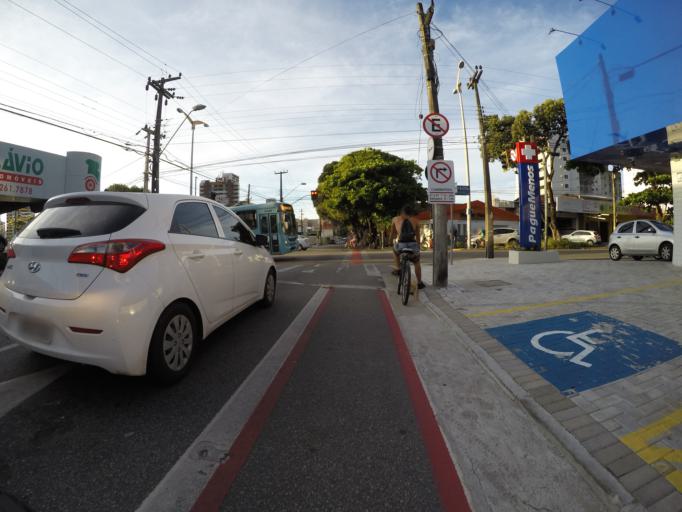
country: BR
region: Ceara
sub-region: Fortaleza
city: Fortaleza
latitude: -3.7378
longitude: -38.5123
